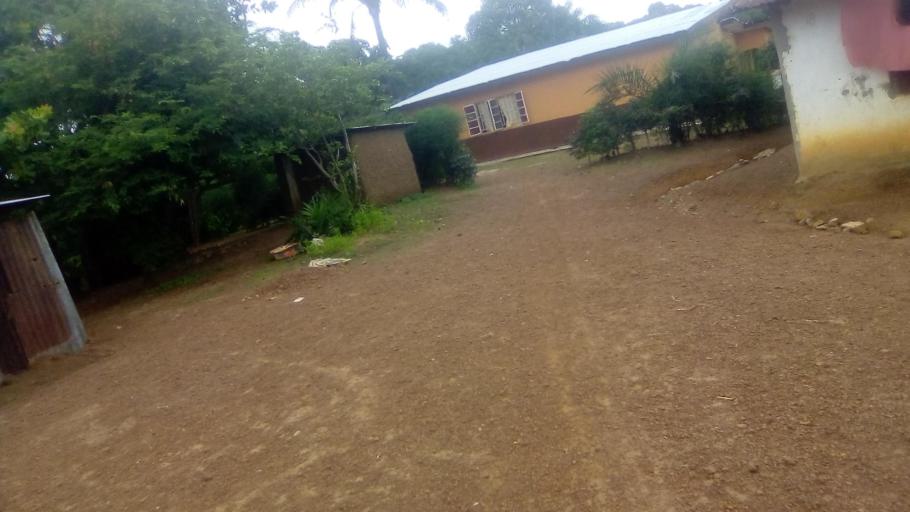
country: SL
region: Southern Province
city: Moyamba
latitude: 8.1559
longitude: -12.4263
